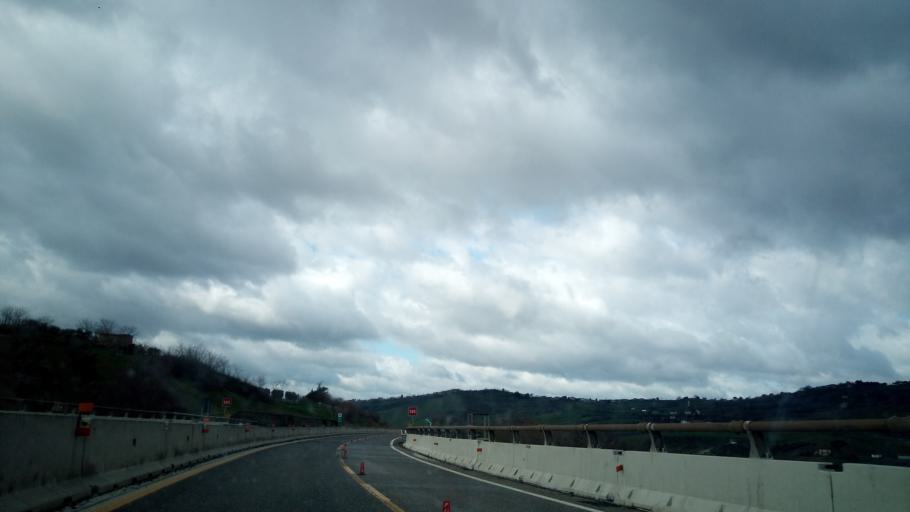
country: IT
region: Campania
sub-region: Provincia di Avellino
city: Flumeri
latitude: 41.0893
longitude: 15.1615
